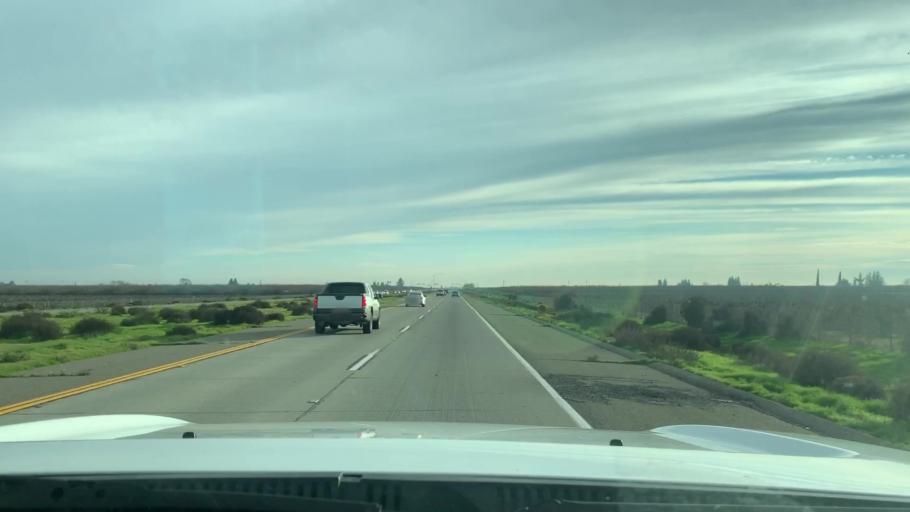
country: US
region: California
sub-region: Fresno County
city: Caruthers
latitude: 36.5250
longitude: -119.7864
